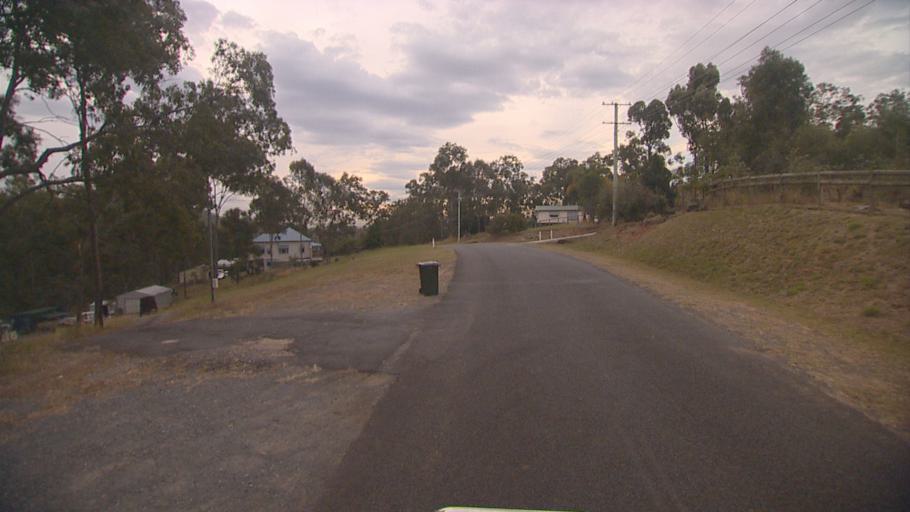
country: AU
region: Queensland
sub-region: Logan
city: Chambers Flat
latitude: -27.8234
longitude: 153.0956
